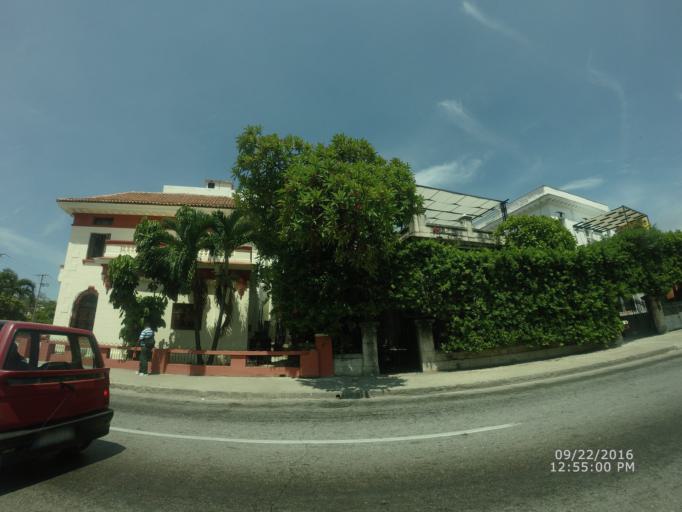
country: CU
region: La Habana
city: Havana
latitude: 23.1435
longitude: -82.3865
